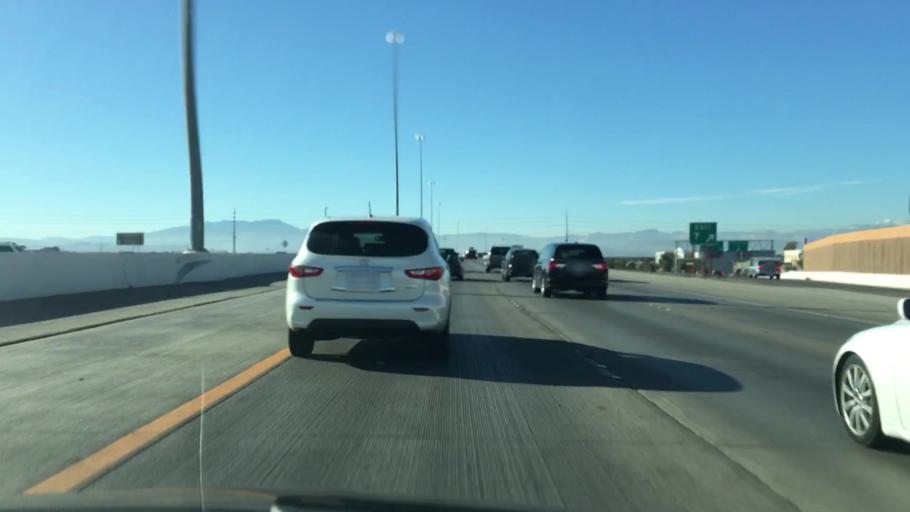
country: US
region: Nevada
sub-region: Clark County
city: Whitney
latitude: 36.0238
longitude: -115.1148
